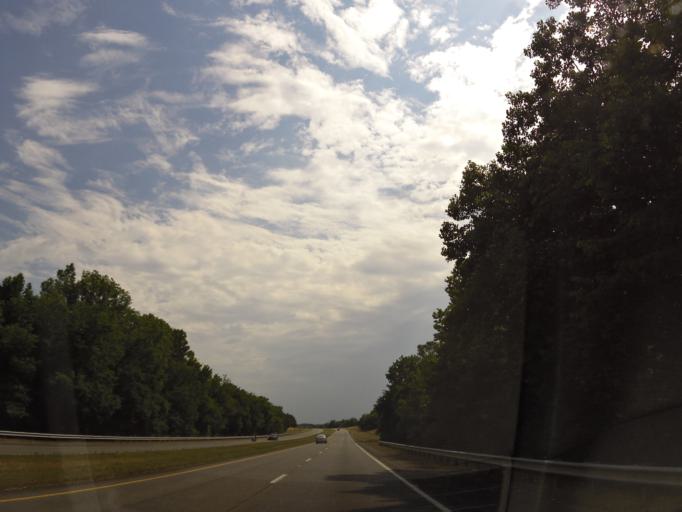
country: US
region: Alabama
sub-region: Jackson County
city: Stevenson
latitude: 34.7645
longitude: -85.9020
